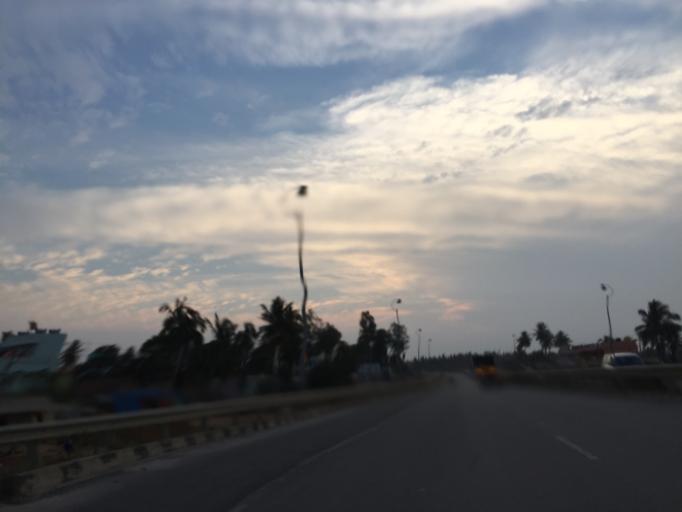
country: IN
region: Karnataka
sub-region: Bangalore Rural
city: Dasarahalli
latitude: 13.1201
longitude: 77.8895
